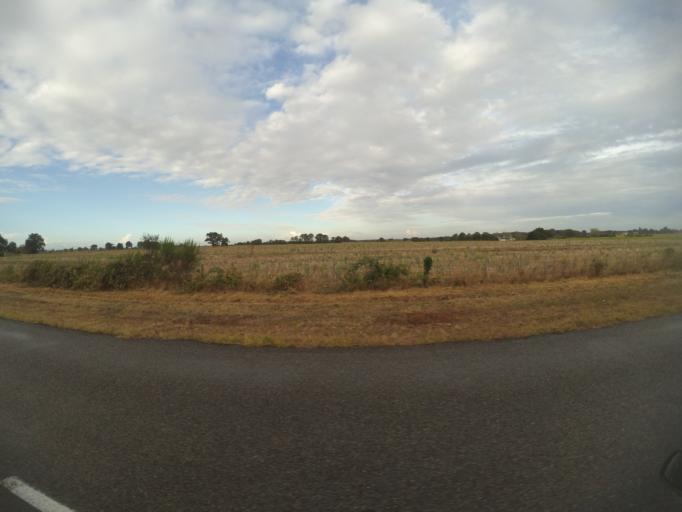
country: FR
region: Pays de la Loire
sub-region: Departement de la Loire-Atlantique
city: La Planche
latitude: 47.0457
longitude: -1.4150
